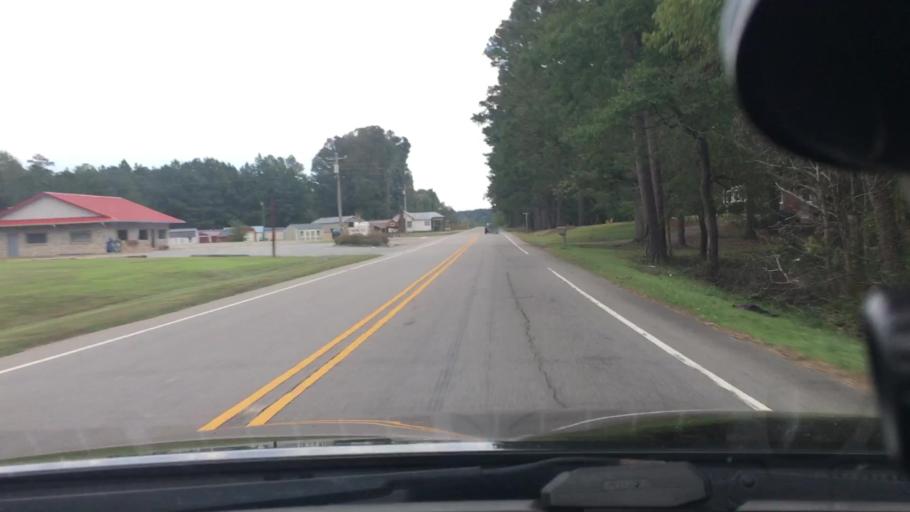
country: US
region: North Carolina
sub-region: Moore County
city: Carthage
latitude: 35.3858
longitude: -79.4956
